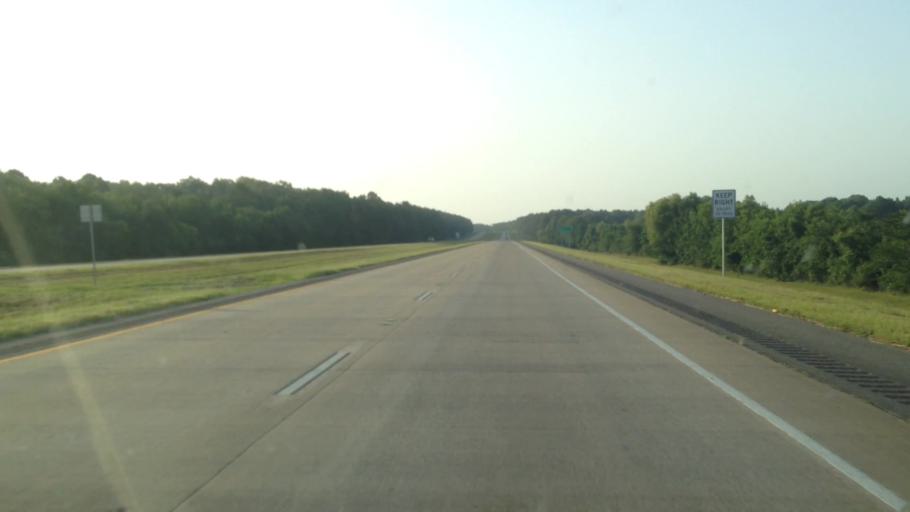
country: US
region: Louisiana
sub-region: Grant Parish
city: Colfax
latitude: 31.4855
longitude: -92.8498
